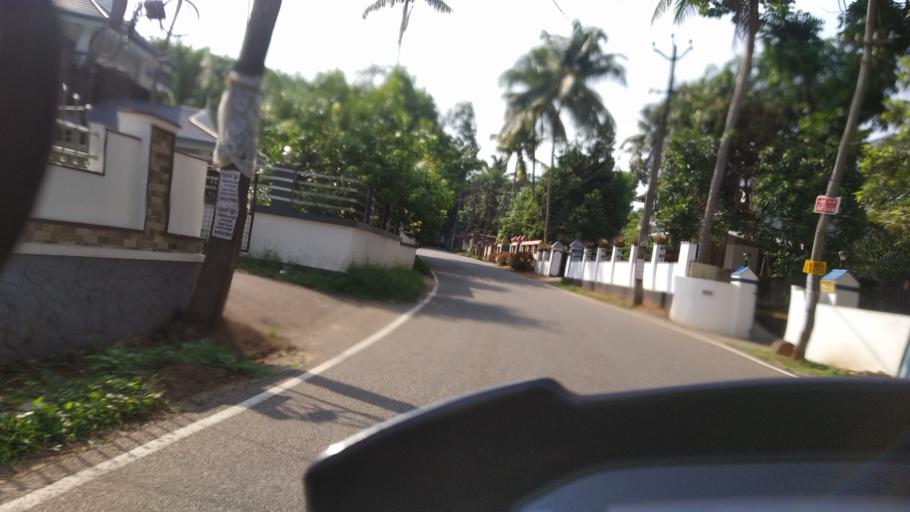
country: IN
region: Kerala
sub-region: Ernakulam
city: Piravam
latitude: 9.8689
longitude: 76.5019
